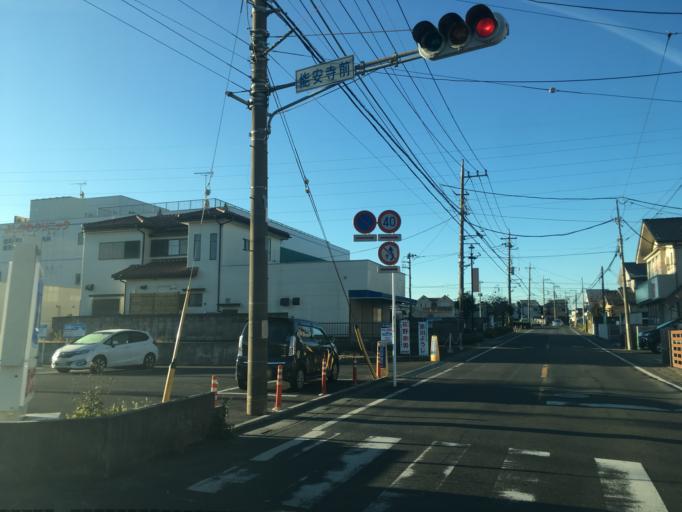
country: JP
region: Saitama
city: Tokorozawa
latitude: 35.8023
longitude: 139.4200
